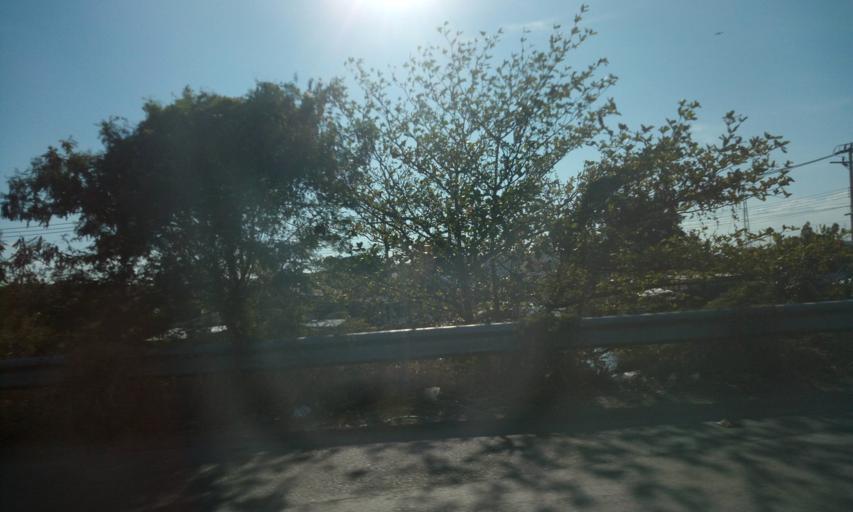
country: TH
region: Samut Prakan
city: Bang Bo District
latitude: 13.5767
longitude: 100.7573
